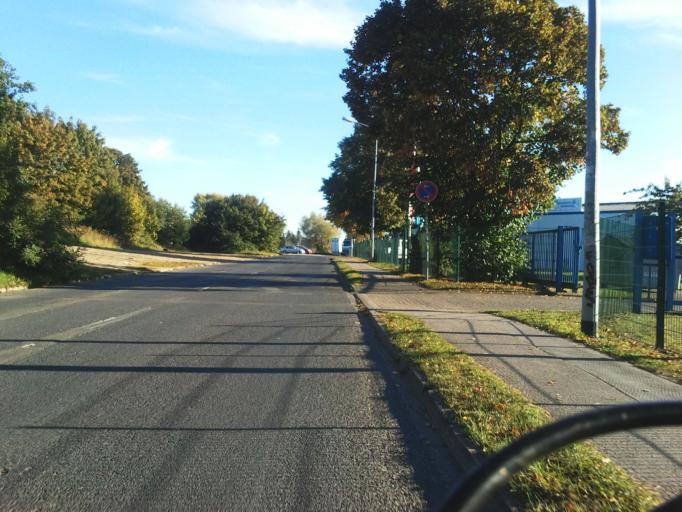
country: DE
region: Mecklenburg-Vorpommern
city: Rostock
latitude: 54.1019
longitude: 12.0894
